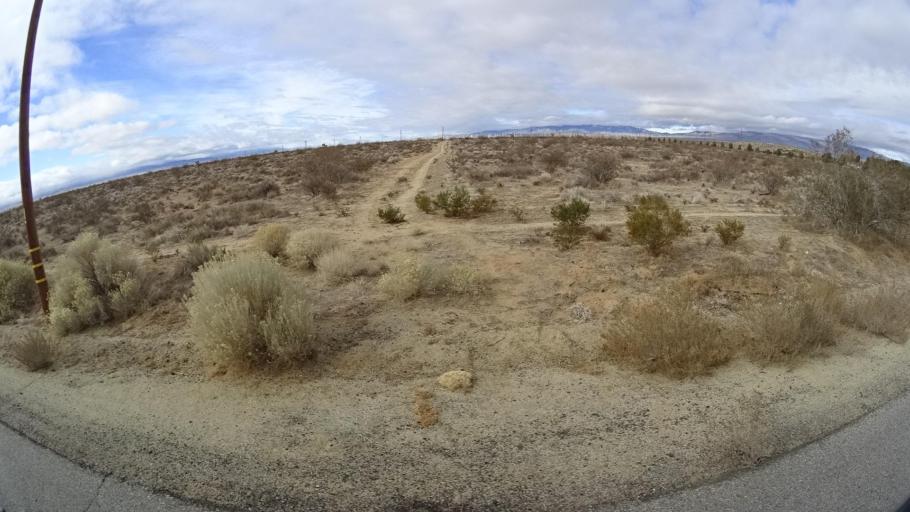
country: US
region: California
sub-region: Kern County
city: Rosamond
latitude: 34.8726
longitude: -118.2911
